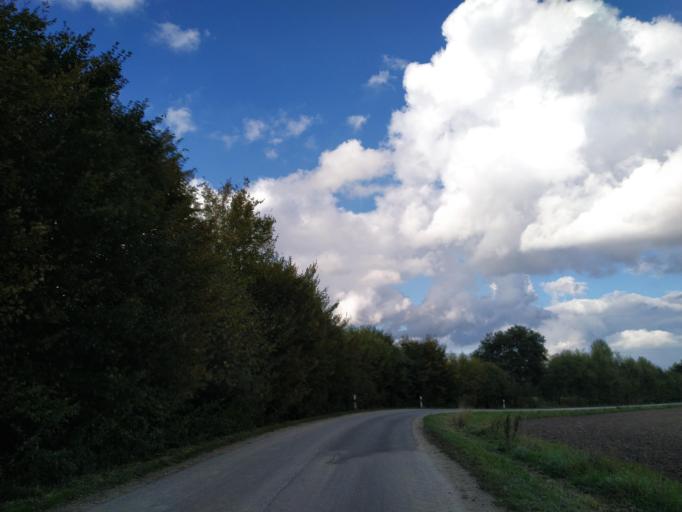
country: DE
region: Schleswig-Holstein
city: Ahrensbok
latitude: 53.9917
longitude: 10.6536
